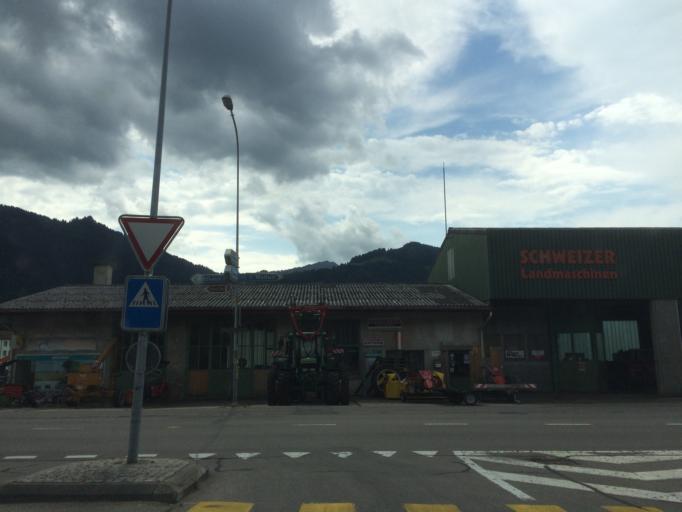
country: CH
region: Saint Gallen
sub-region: Wahlkreis Toggenburg
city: Krummenau
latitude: 47.2313
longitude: 9.1920
